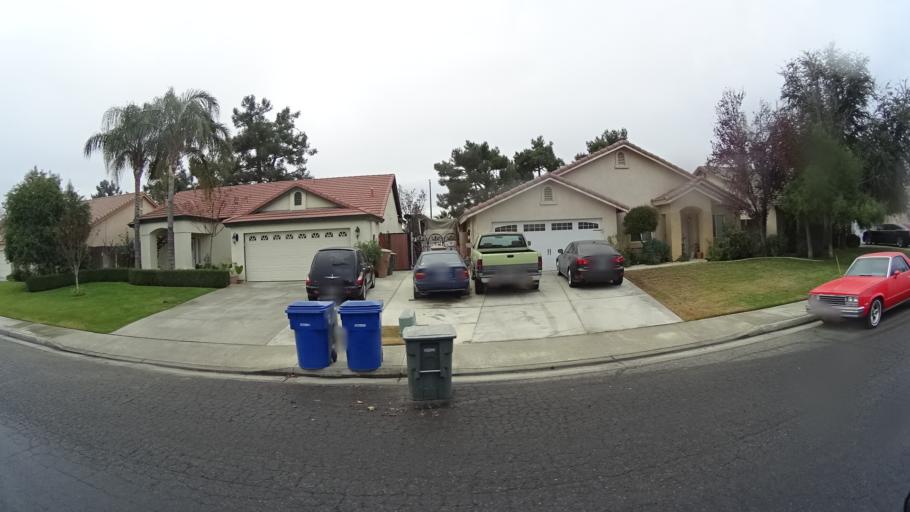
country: US
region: California
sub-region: Kern County
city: Greenfield
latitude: 35.3038
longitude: -119.0763
